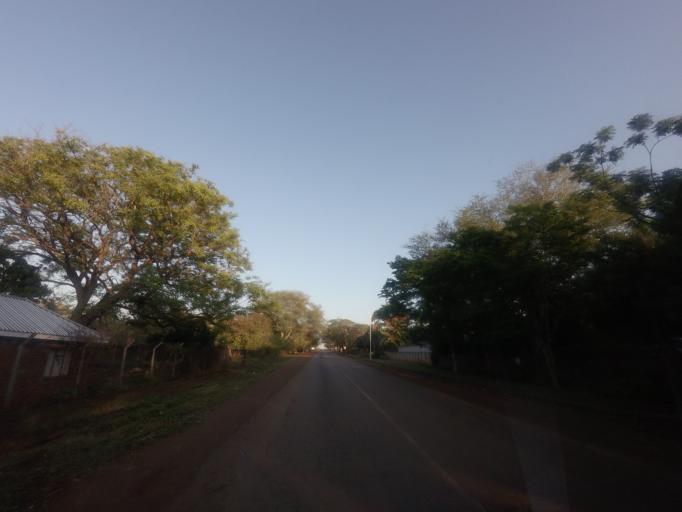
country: ZA
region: Mpumalanga
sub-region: Ehlanzeni District
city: Komatipoort
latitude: -25.4319
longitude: 31.9521
